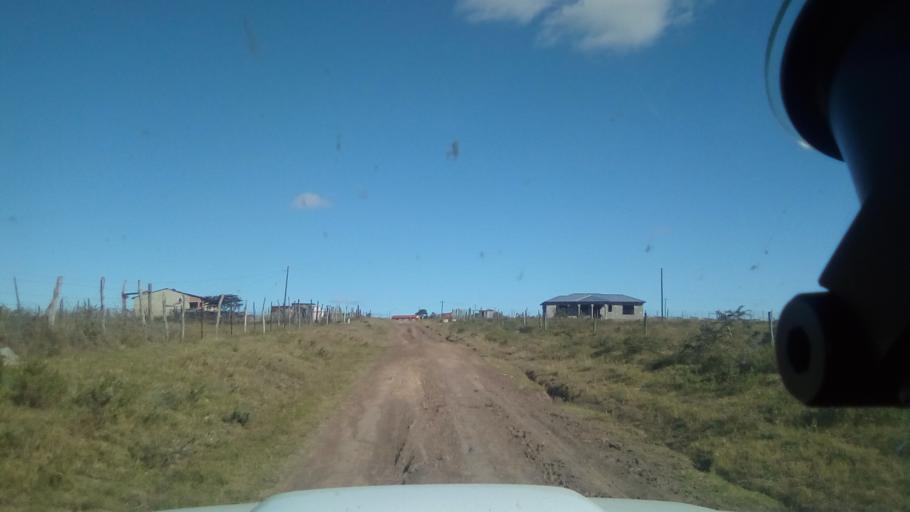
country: ZA
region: Eastern Cape
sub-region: Buffalo City Metropolitan Municipality
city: Bhisho
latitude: -32.7795
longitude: 27.3384
